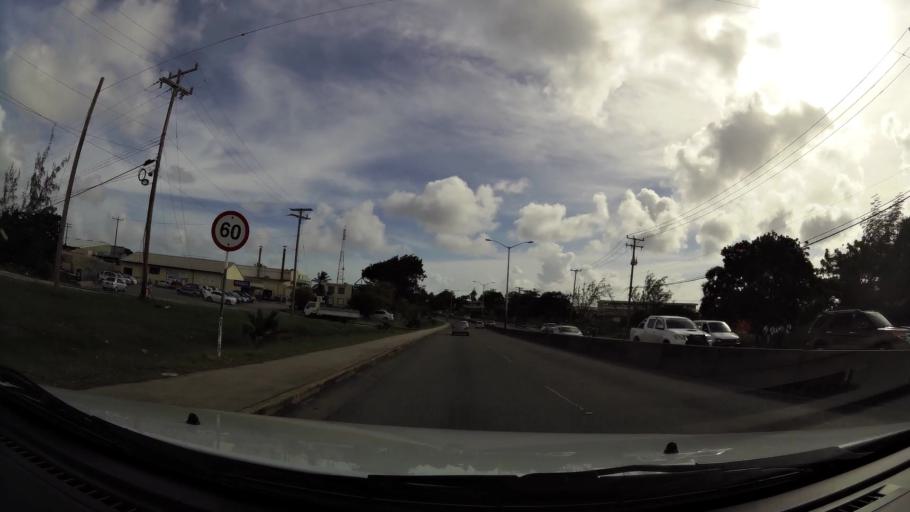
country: BB
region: Saint Michael
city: Bridgetown
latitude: 13.1003
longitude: -59.5801
